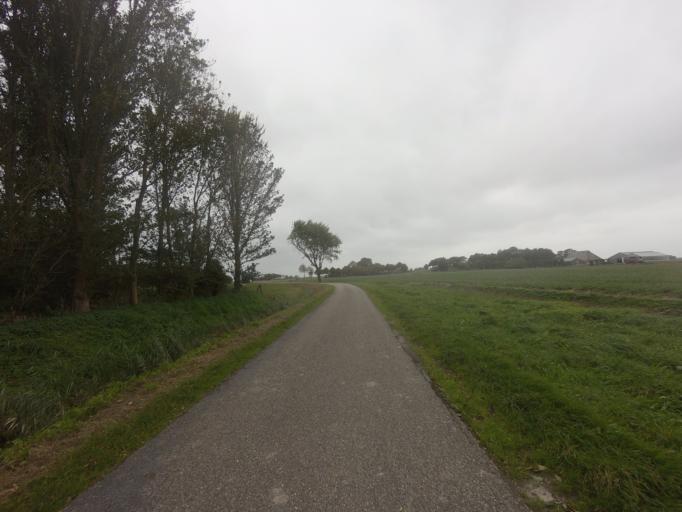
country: NL
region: Friesland
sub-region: Gemeente Ferwerderadiel
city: Ferwert
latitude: 53.3371
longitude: 5.8568
